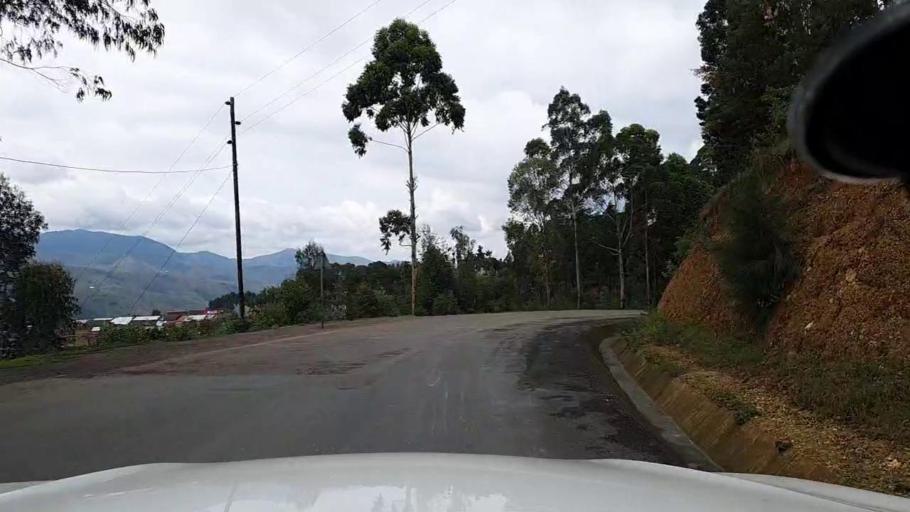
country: RW
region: Western Province
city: Kibuye
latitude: -2.0674
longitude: 29.5390
